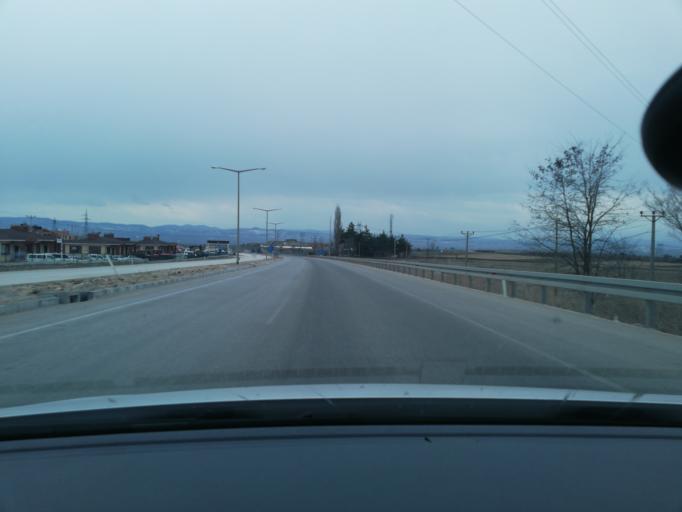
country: TR
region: Bolu
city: Gerede
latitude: 40.7859
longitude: 32.2100
